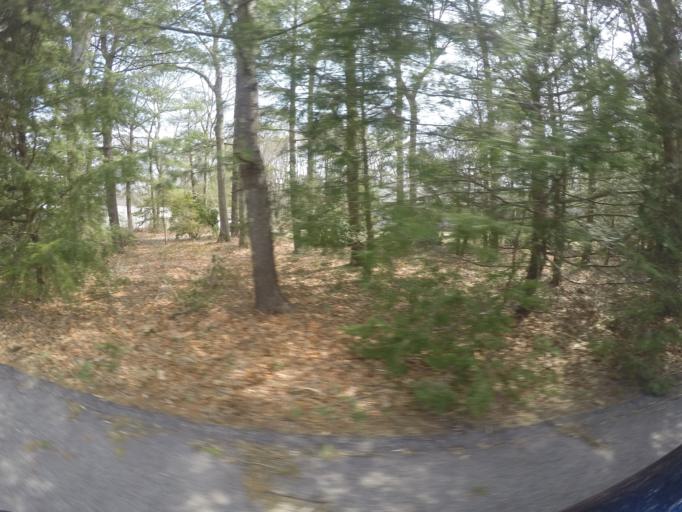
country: US
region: Massachusetts
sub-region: Bristol County
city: Easton
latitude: 42.0442
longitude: -71.1073
